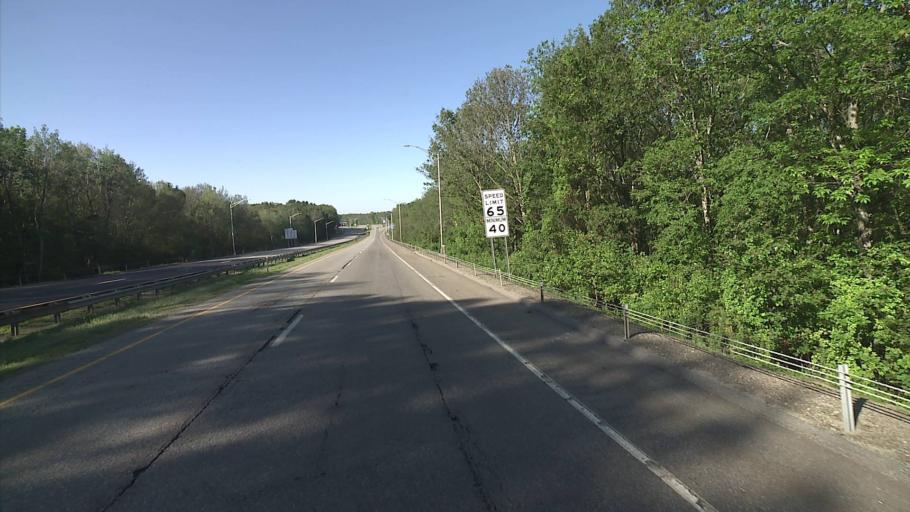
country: US
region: Connecticut
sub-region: Windham County
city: Wauregan
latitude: 41.7594
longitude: -71.8747
